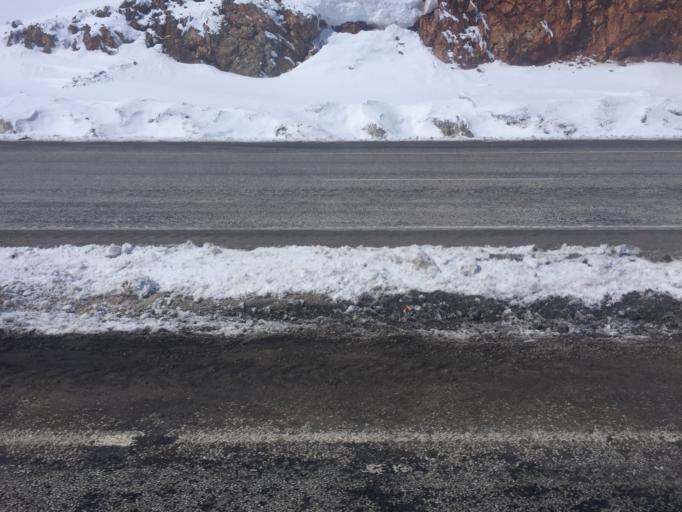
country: TR
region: Kahramanmaras
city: Goksun
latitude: 38.1895
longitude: 36.4569
